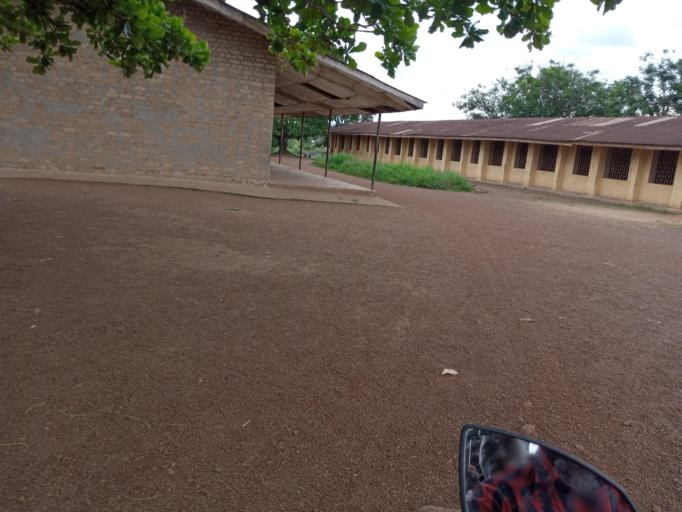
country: SL
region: Southern Province
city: Largo
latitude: 8.1138
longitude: -12.0613
